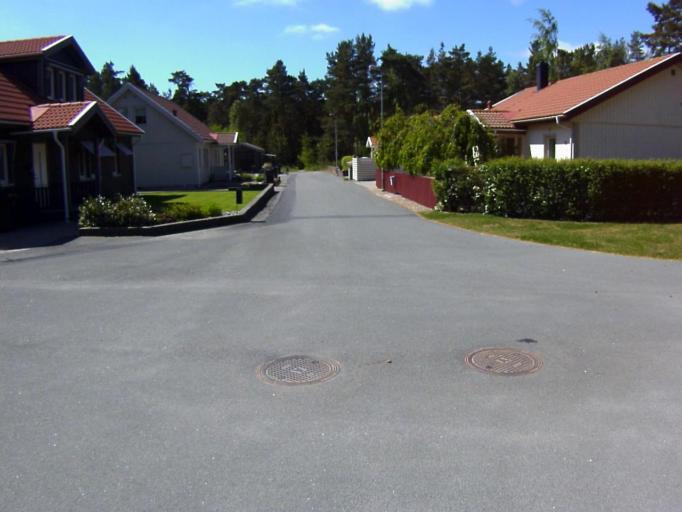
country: SE
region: Skane
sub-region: Kristianstads Kommun
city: Ahus
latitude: 55.9414
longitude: 14.3005
